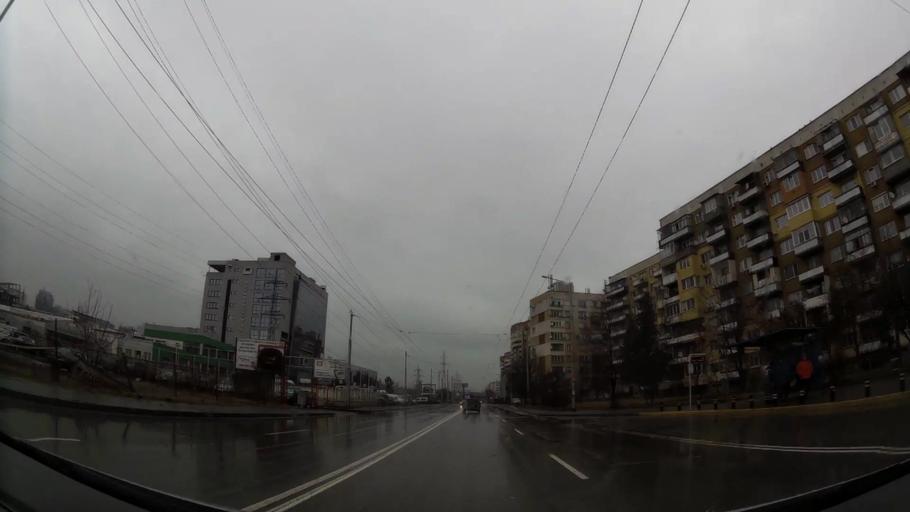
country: BG
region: Sofia-Capital
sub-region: Stolichna Obshtina
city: Sofia
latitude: 42.6606
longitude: 23.3941
